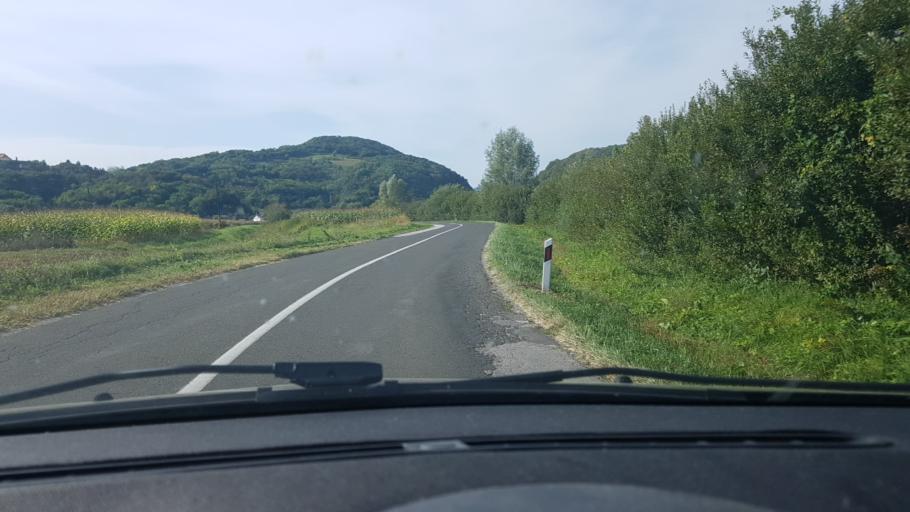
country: HR
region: Krapinsko-Zagorska
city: Zlatar
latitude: 46.1021
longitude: 16.0222
